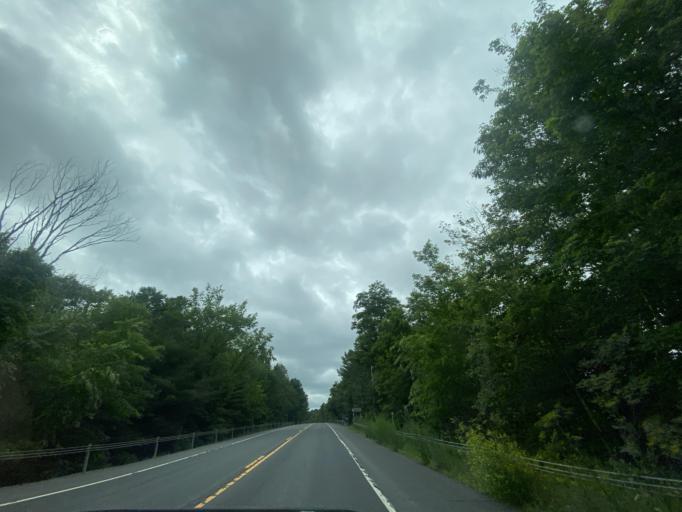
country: US
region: New York
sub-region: Greene County
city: Cairo
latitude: 42.3939
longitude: -73.9550
